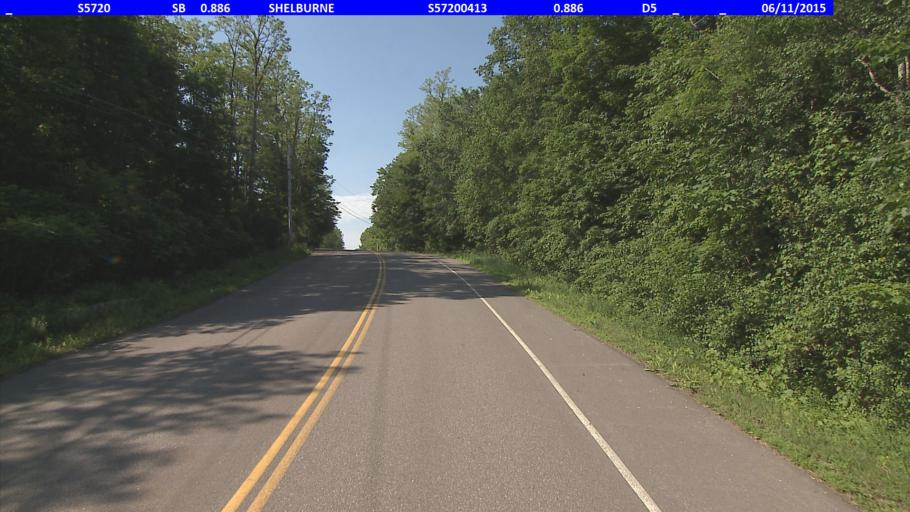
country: US
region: Vermont
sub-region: Chittenden County
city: South Burlington
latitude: 44.3808
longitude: -73.2020
